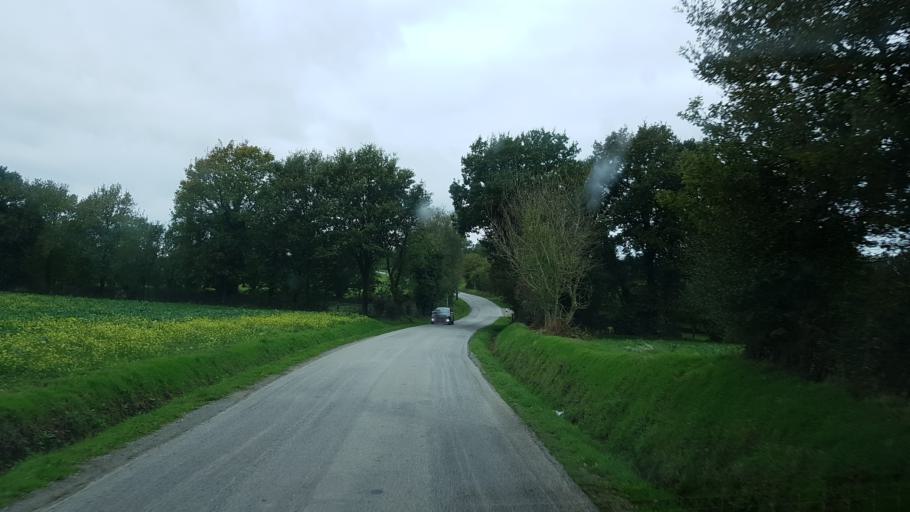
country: FR
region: Brittany
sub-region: Departement du Morbihan
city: Serent
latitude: 47.7806
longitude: -2.4797
